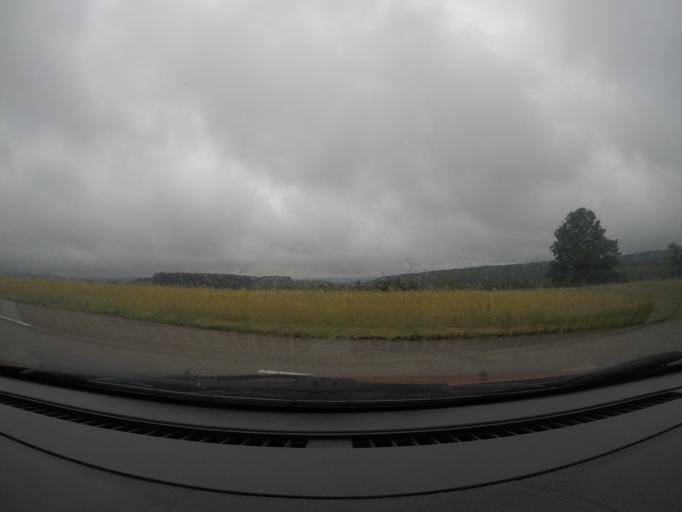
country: RS
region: Central Serbia
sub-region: Belgrade
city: Sopot
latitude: 44.5146
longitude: 20.5374
